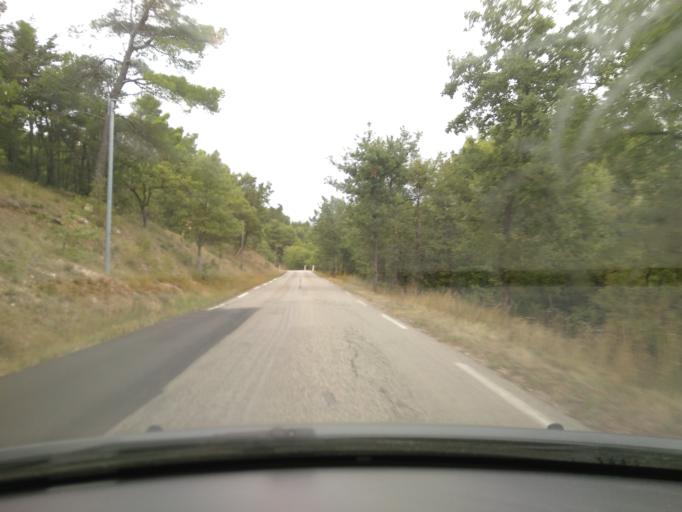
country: FR
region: Provence-Alpes-Cote d'Azur
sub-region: Departement du Vaucluse
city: Valreas
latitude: 44.3659
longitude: 5.0094
